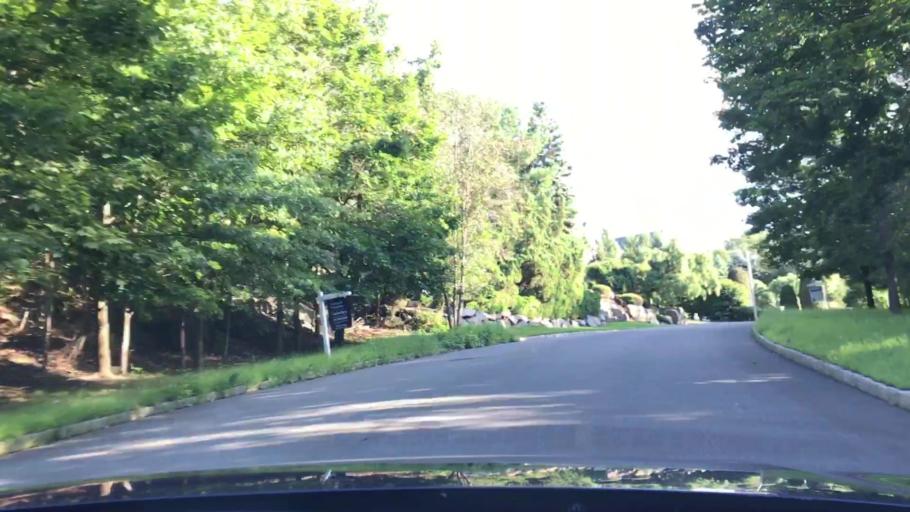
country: US
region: New Jersey
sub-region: Bergen County
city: Cresskill
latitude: 40.9315
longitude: -73.9435
